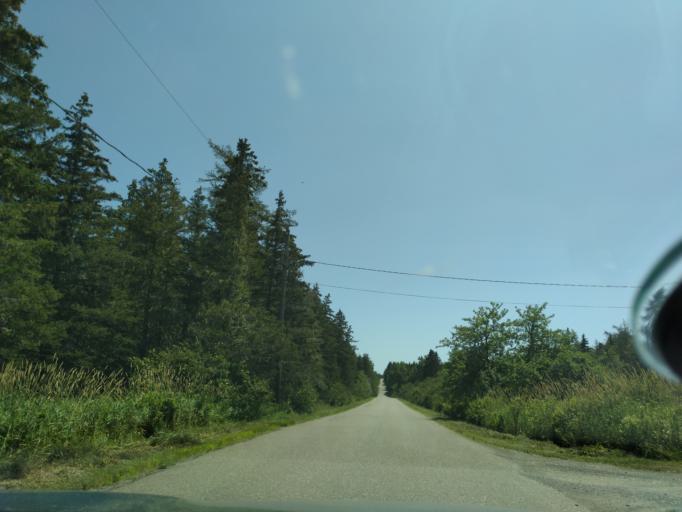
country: US
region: Maine
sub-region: Washington County
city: Eastport
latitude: 44.8371
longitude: -67.0117
